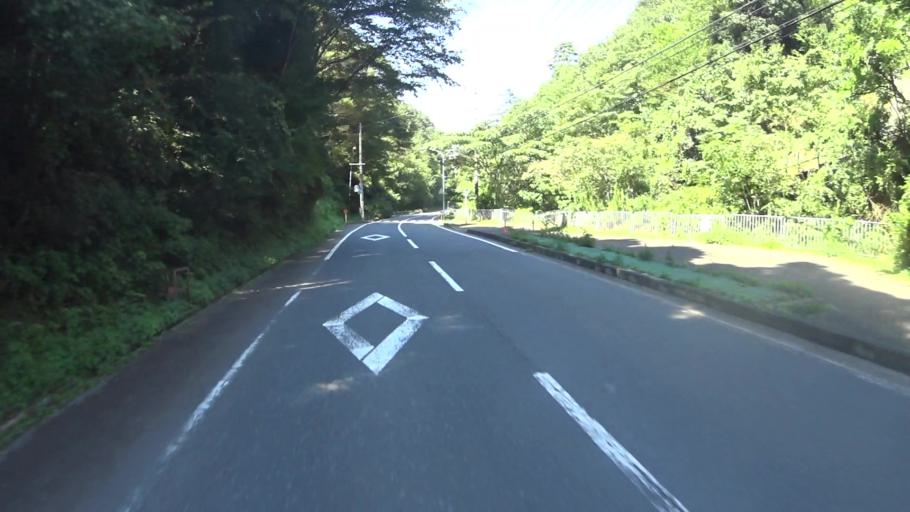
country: JP
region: Kyoto
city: Kameoka
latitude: 34.9494
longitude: 135.5223
